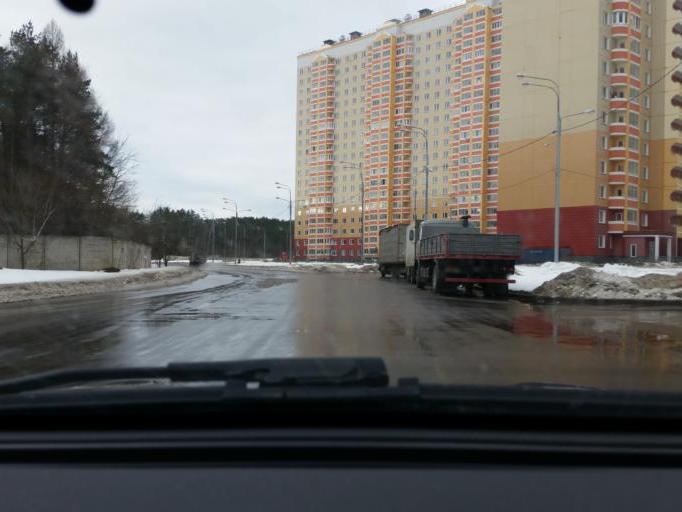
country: RU
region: Moskovskaya
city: Shcherbinka
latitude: 55.5199
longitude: 37.5949
